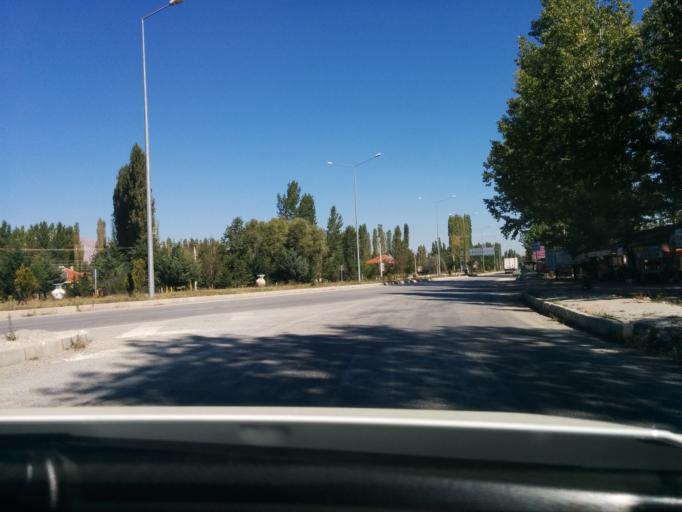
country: TR
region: Antalya
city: Kizilcadag
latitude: 37.0214
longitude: 29.8201
